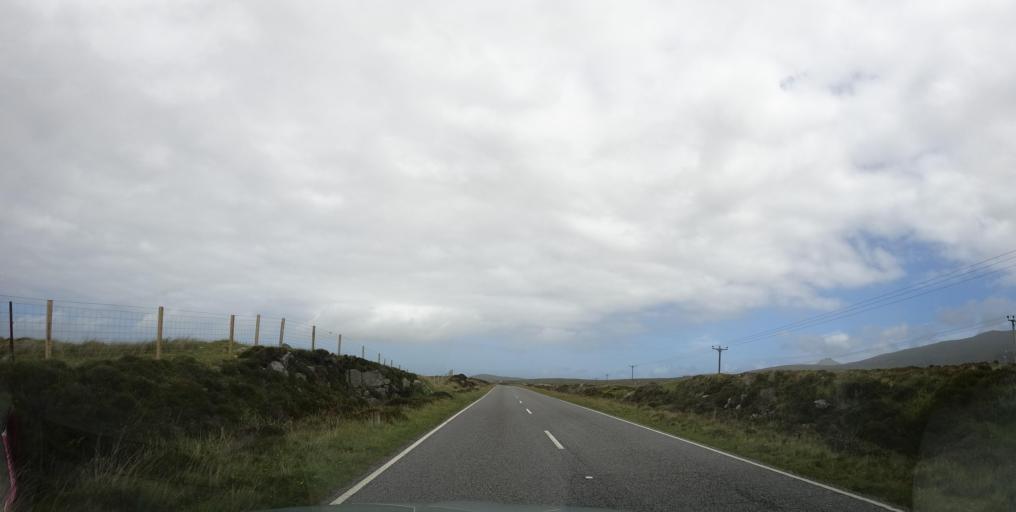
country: GB
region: Scotland
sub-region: Eilean Siar
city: Isle of South Uist
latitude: 57.2537
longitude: -7.3757
